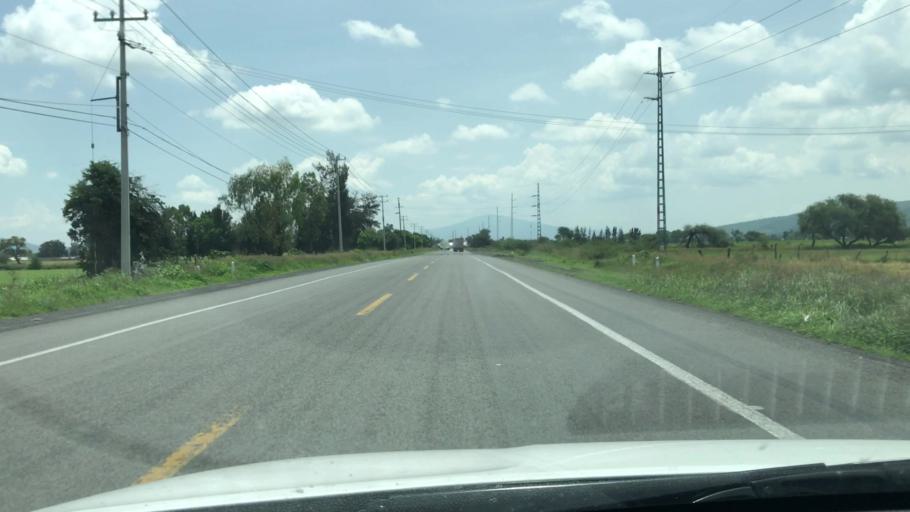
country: MX
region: Michoacan
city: Tanhuato de Guerrero
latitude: 20.2814
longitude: -102.3522
